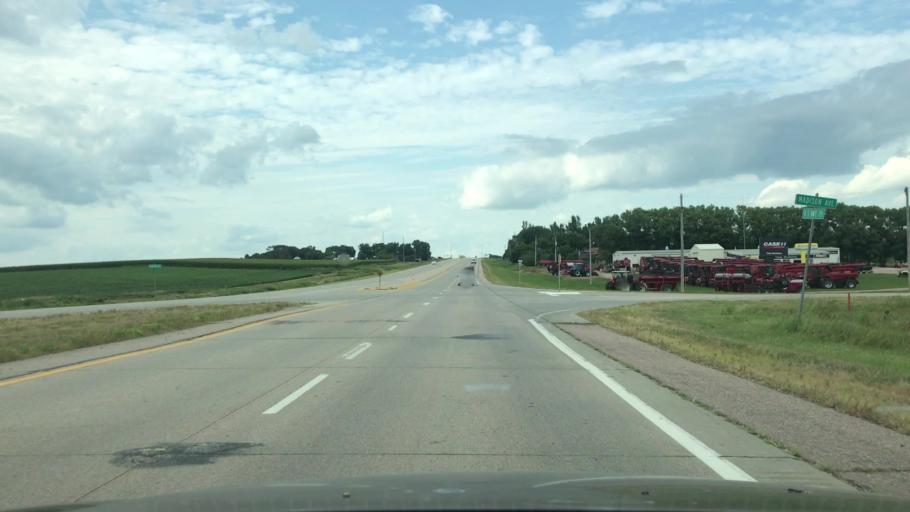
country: US
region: Iowa
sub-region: Plymouth County
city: Le Mars
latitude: 42.8088
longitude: -96.1747
